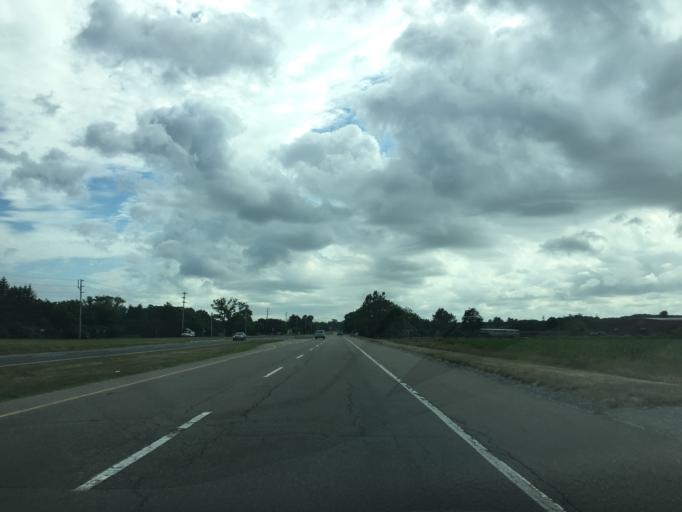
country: US
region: New York
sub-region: Suffolk County
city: Southold
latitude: 41.0580
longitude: -72.4497
